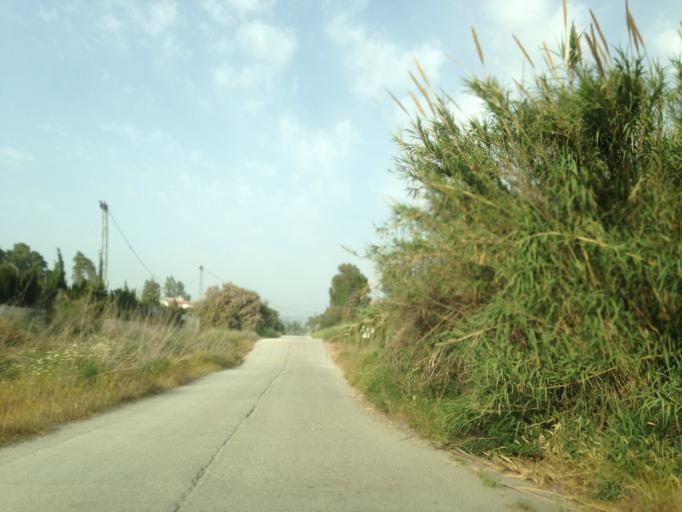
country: ES
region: Andalusia
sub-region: Provincia de Malaga
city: Estacion de Cartama
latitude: 36.7505
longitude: -4.5634
